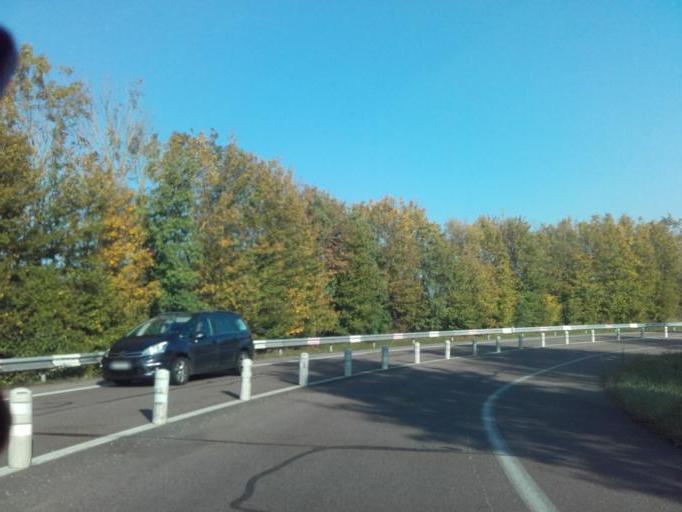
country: FR
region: Bourgogne
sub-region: Departement de Saone-et-Loire
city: Chatenoy-le-Royal
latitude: 46.8051
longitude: 4.8242
